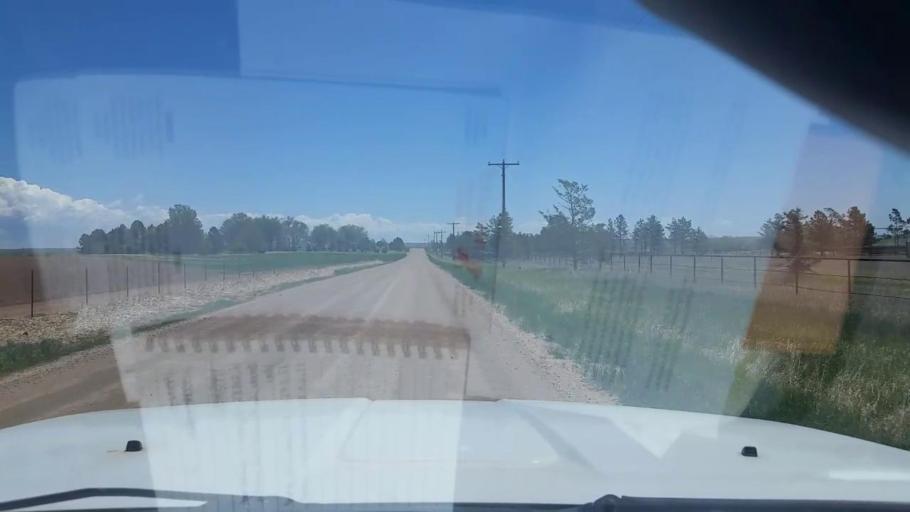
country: US
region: Colorado
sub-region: Larimer County
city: Wellington
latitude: 40.7981
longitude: -105.0616
